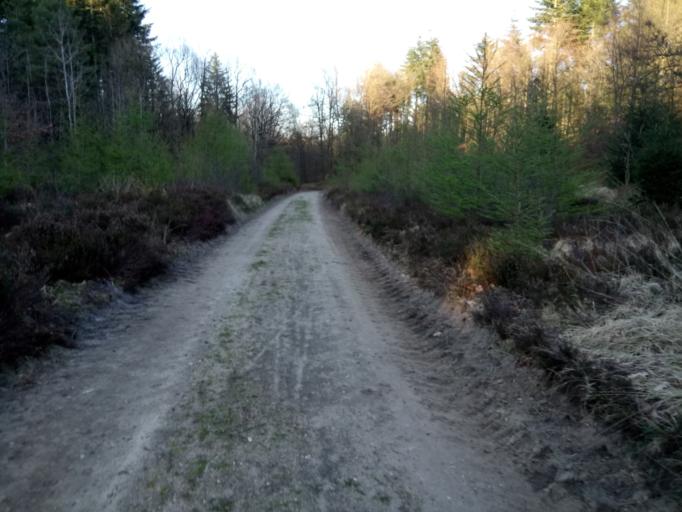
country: DK
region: Central Jutland
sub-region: Ringkobing-Skjern Kommune
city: Skjern
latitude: 56.0052
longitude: 8.4550
